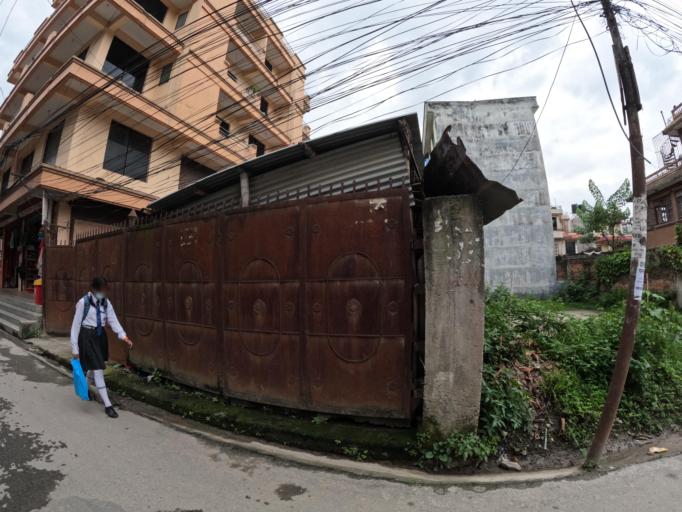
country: NP
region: Central Region
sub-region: Bagmati Zone
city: Kathmandu
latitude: 27.7434
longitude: 85.3221
